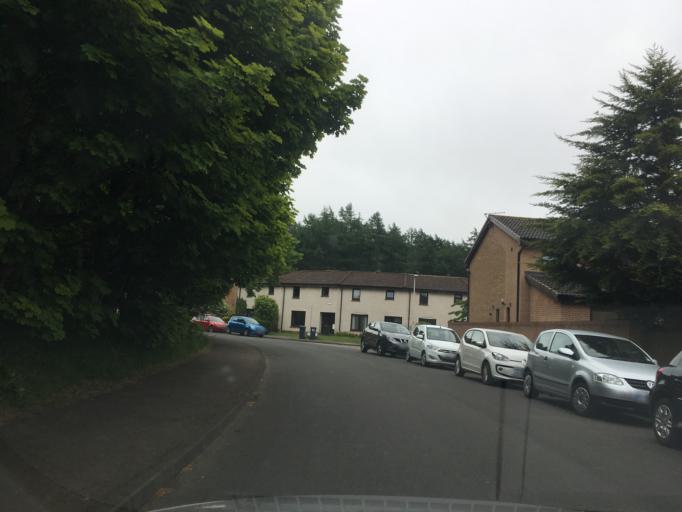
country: GB
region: Scotland
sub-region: Midlothian
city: Loanhead
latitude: 55.9041
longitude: -3.1977
